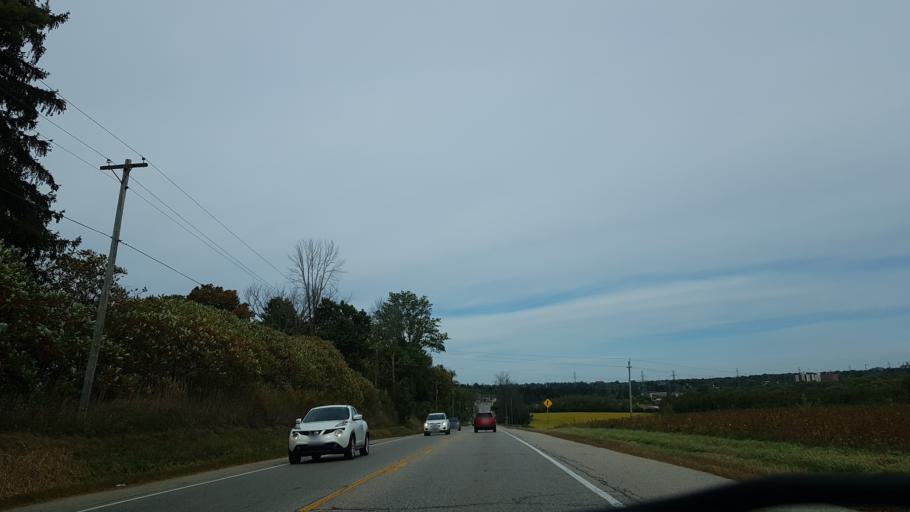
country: CA
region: Ontario
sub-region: Wellington County
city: Guelph
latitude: 43.5109
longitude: -80.2666
